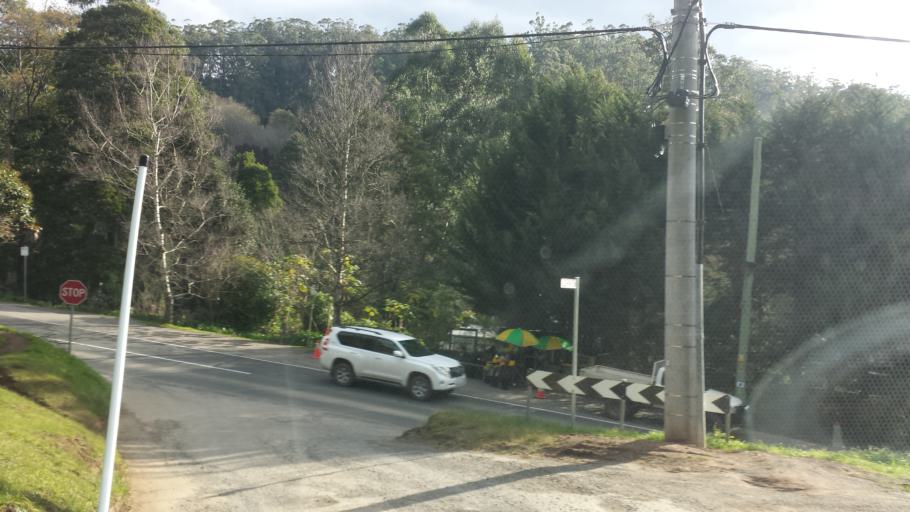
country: AU
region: Victoria
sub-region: Yarra Ranges
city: Kallista
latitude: -37.8819
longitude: 145.3718
